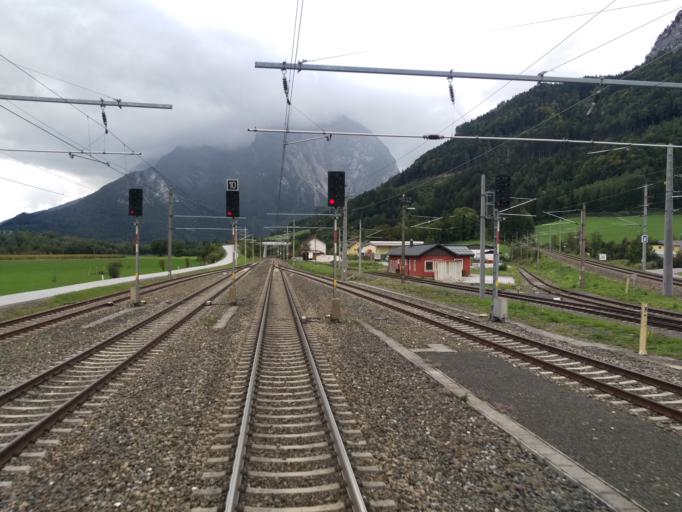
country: AT
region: Styria
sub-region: Politischer Bezirk Liezen
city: Stainach
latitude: 47.5289
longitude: 14.1020
